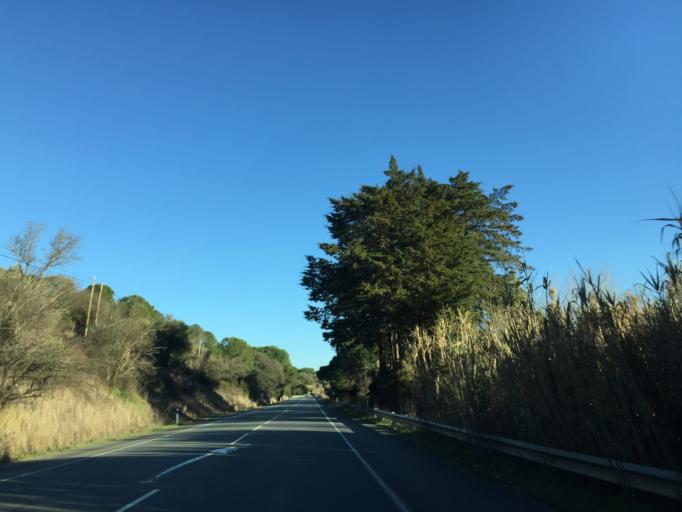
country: PT
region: Setubal
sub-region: Grandola
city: Grandola
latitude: 38.1259
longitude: -8.4604
